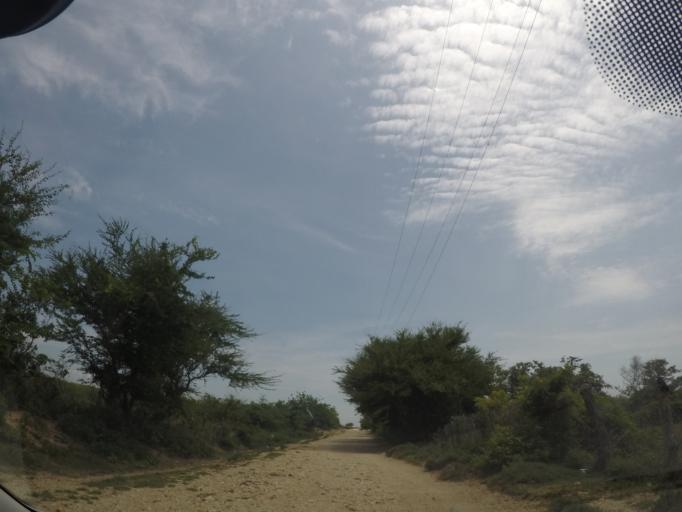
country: MX
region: Oaxaca
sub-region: San Mateo del Mar
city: Colonia Juarez
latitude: 16.2109
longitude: -95.0357
